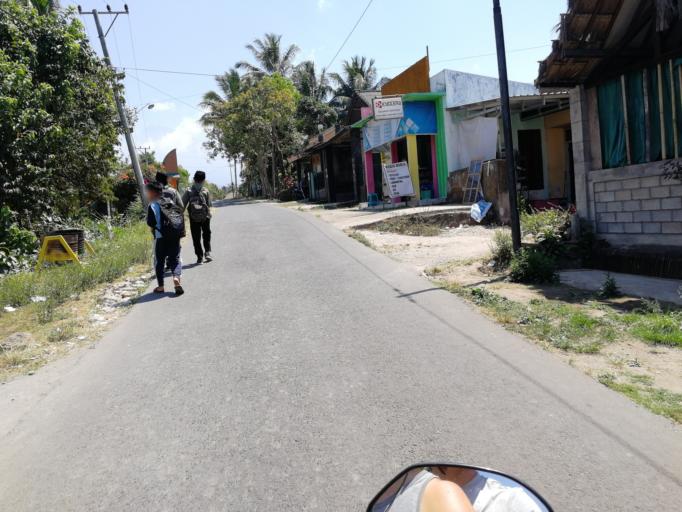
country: ID
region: West Nusa Tenggara
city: Tetebatu
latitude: -8.5610
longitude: 116.4195
